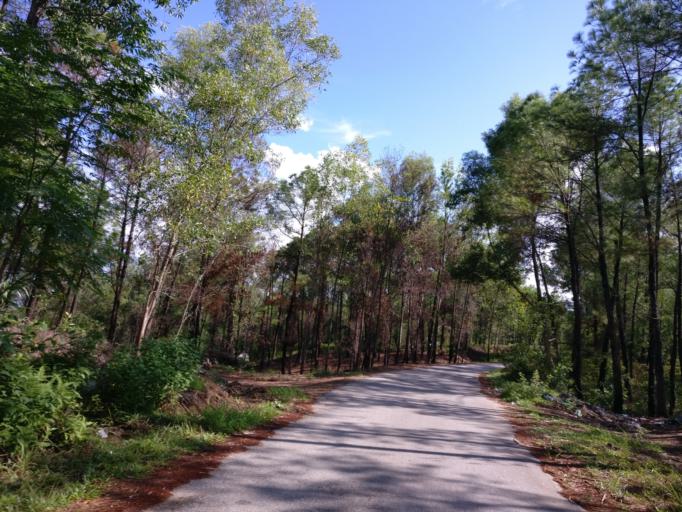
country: VN
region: Thua Thien-Hue
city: Hue
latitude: 16.4087
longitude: 107.5937
